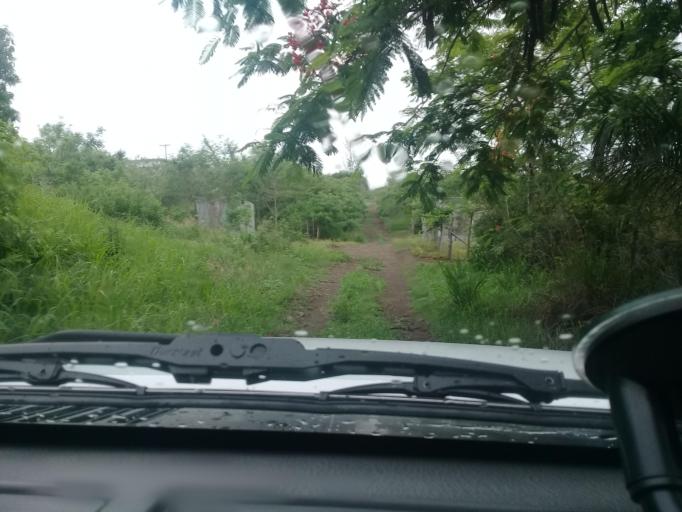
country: MX
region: Veracruz
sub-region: Puente Nacional
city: Cabezas
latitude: 19.3657
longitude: -96.3996
